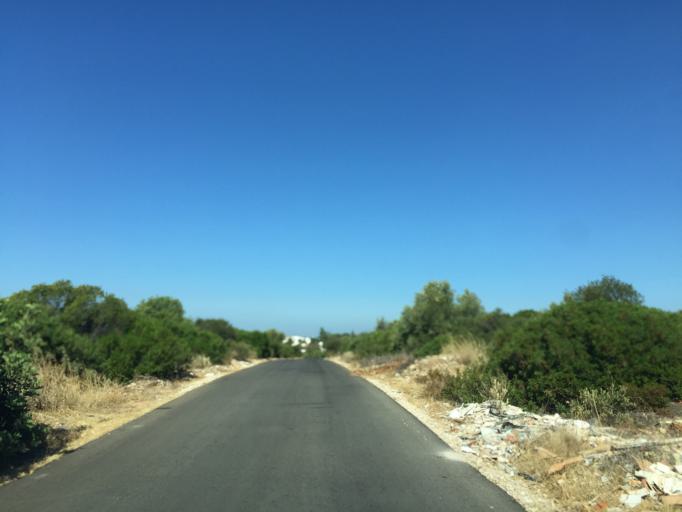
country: PT
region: Faro
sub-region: Loule
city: Almancil
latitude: 37.0983
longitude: -8.0336
